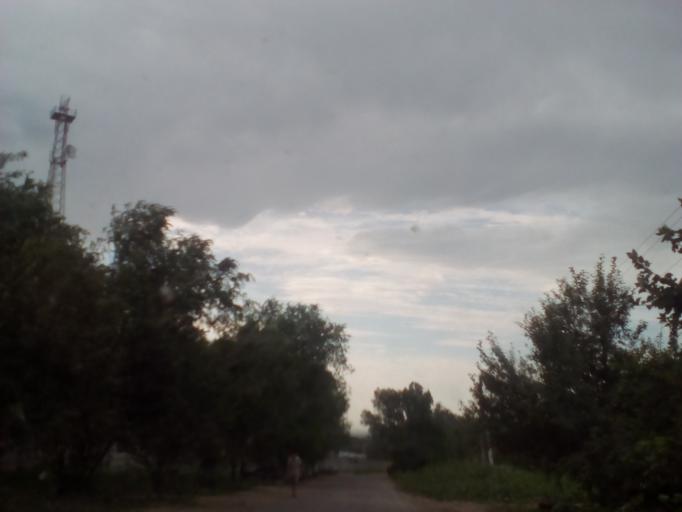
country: KZ
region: Almaty Oblysy
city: Burunday
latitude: 43.1586
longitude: 76.3834
